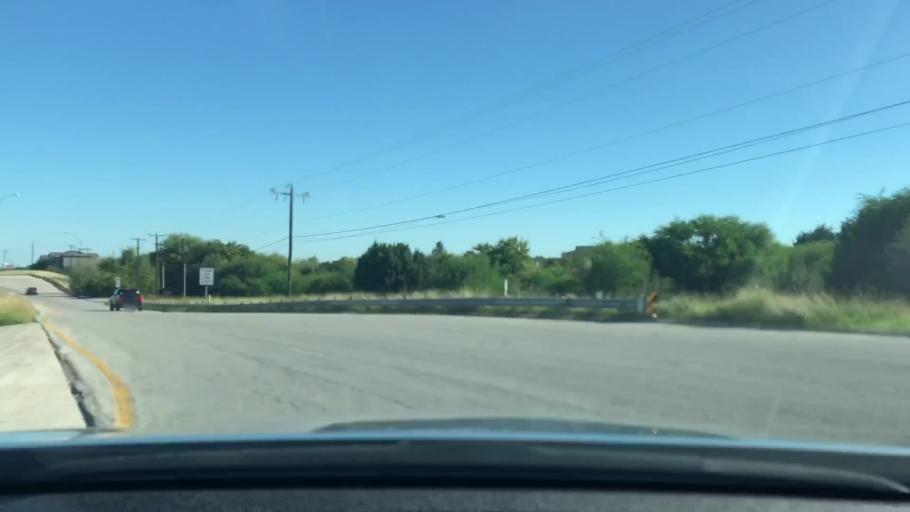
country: US
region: Texas
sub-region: Bexar County
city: Universal City
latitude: 29.5461
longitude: -98.3156
